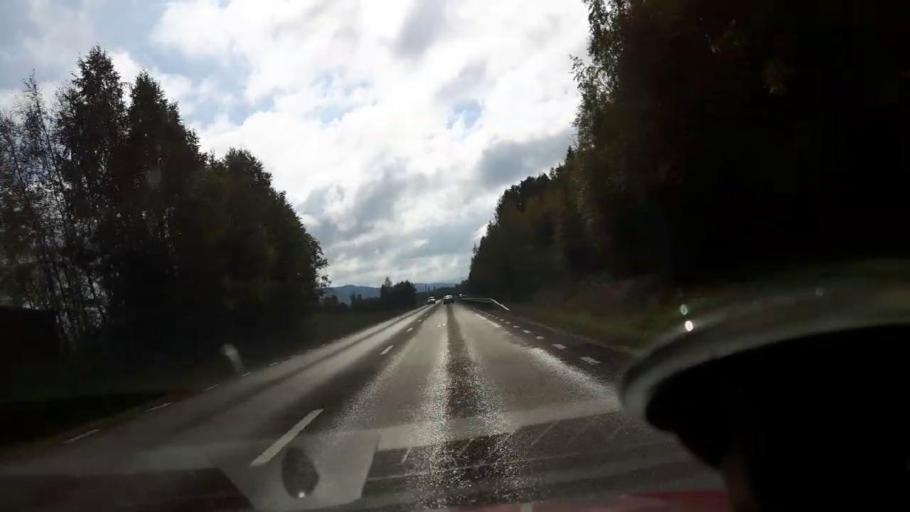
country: SE
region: Gaevleborg
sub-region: Ljusdals Kommun
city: Jaervsoe
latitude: 61.7320
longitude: 16.1646
